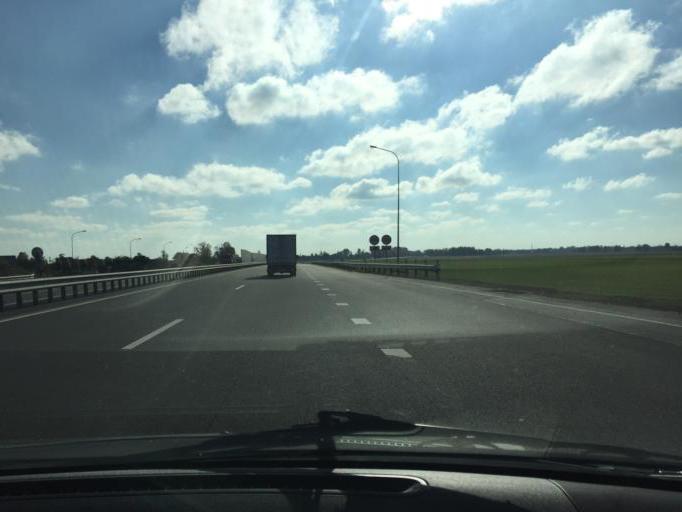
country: BY
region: Minsk
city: Slutsk
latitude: 53.1033
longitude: 27.5698
